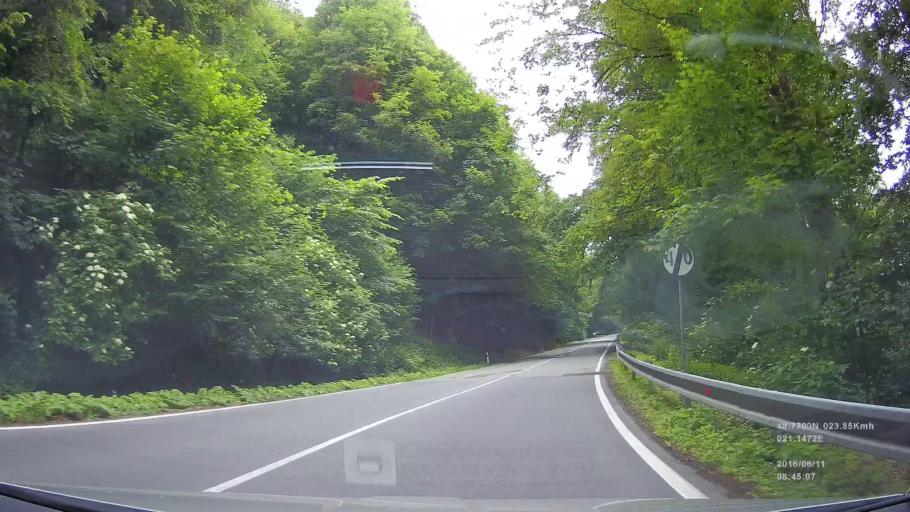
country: SK
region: Kosicky
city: Kosice
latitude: 48.7711
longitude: 21.1534
